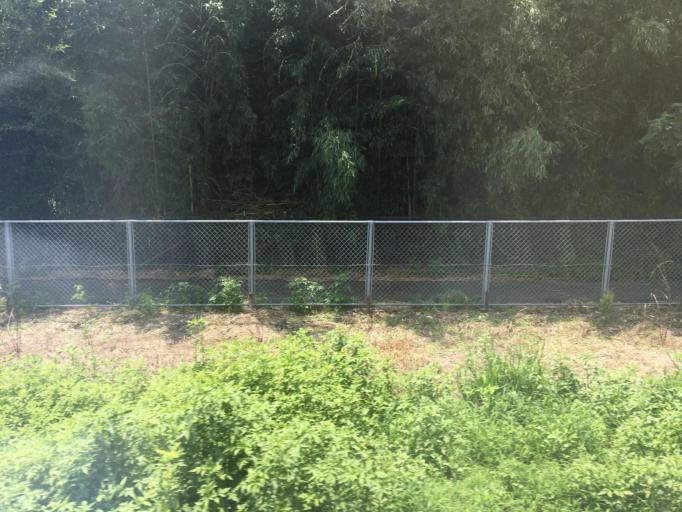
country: JP
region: Gunma
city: Tatebayashi
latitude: 36.2489
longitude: 139.5038
